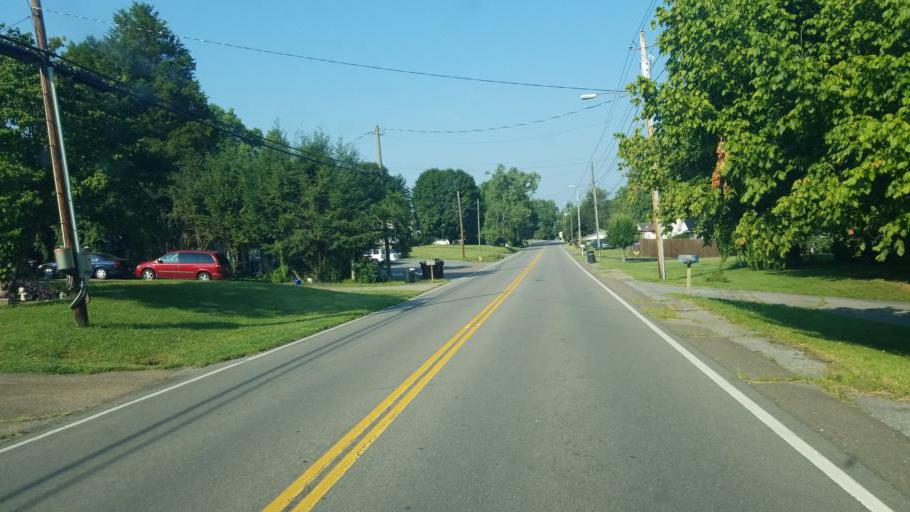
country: US
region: Tennessee
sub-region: Sullivan County
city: Bluff City
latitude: 36.4709
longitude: -82.2713
